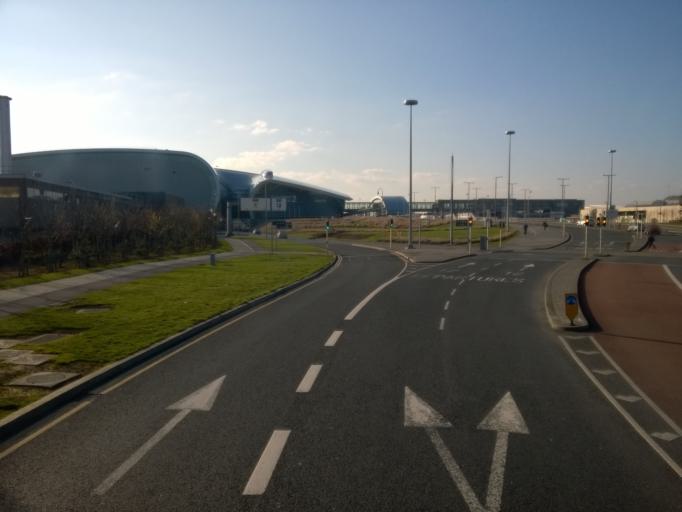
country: IE
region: Leinster
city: Beaumont
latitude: 53.4249
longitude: -6.2356
